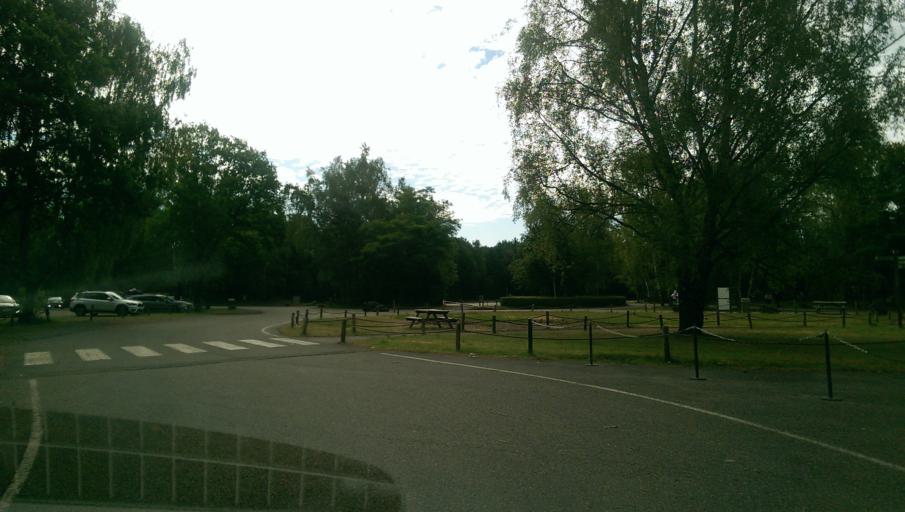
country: NL
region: North Brabant
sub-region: Gemeente Tilburg
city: Tilburg
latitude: 51.5249
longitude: 5.1150
